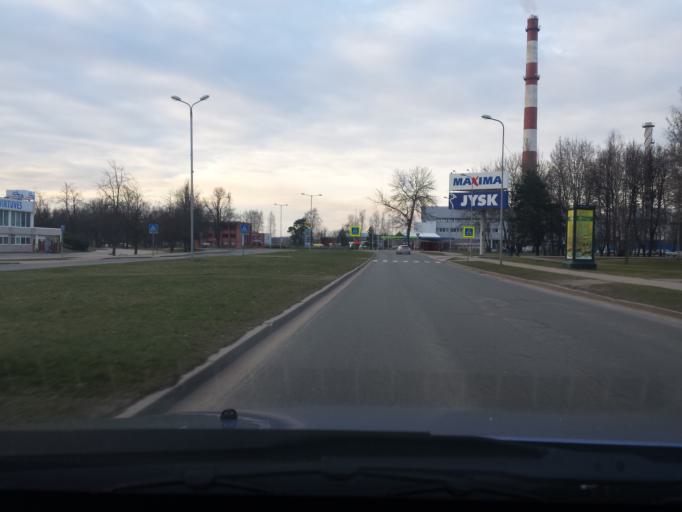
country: LV
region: Marupe
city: Marupe
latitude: 56.9597
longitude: 24.0352
